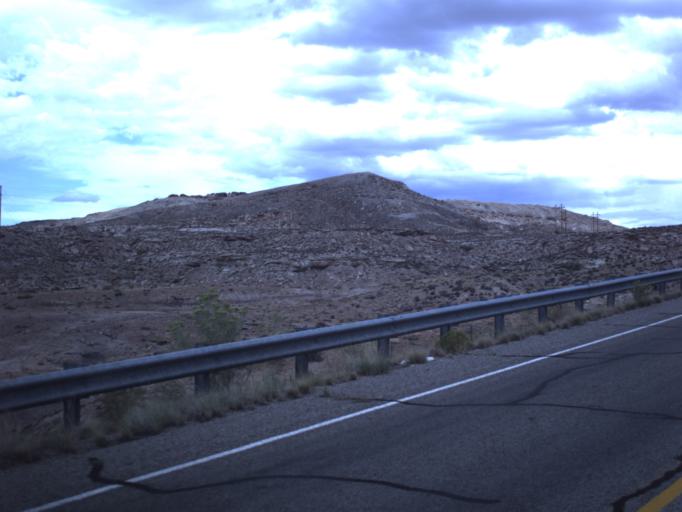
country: US
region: Utah
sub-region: San Juan County
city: Blanding
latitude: 37.2744
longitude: -109.3517
